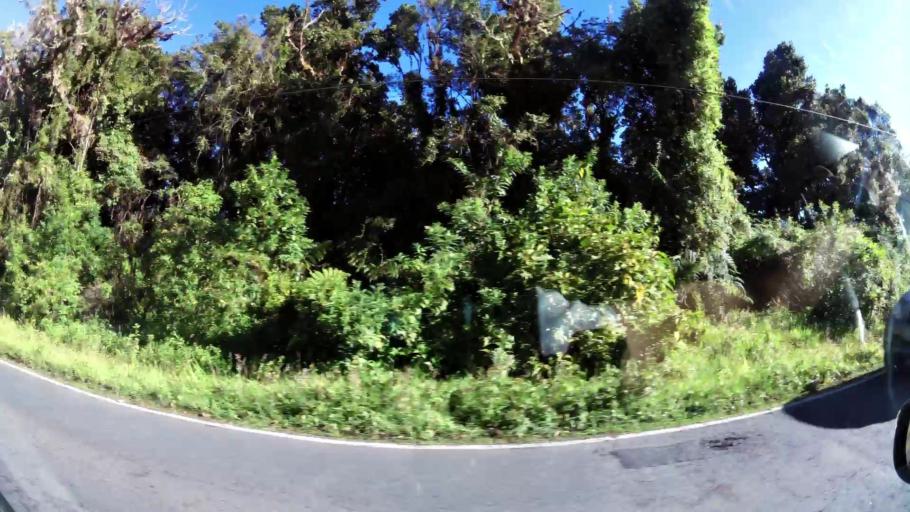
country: CR
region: San Jose
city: San Marcos
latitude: 9.6972
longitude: -83.9299
